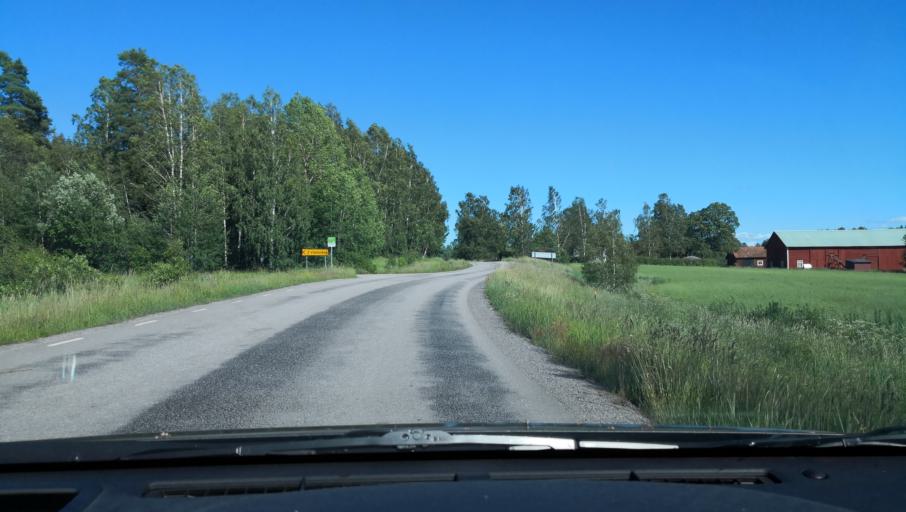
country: SE
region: Soedermanland
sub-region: Eskilstuna Kommun
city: Arla
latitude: 59.3235
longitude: 16.6152
